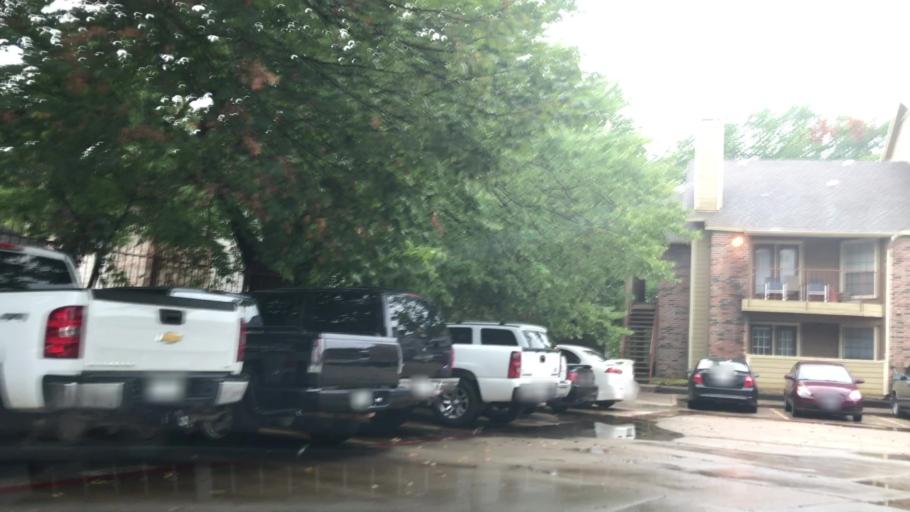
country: US
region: Texas
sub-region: Denton County
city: Lewisville
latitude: 33.0174
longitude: -96.9890
